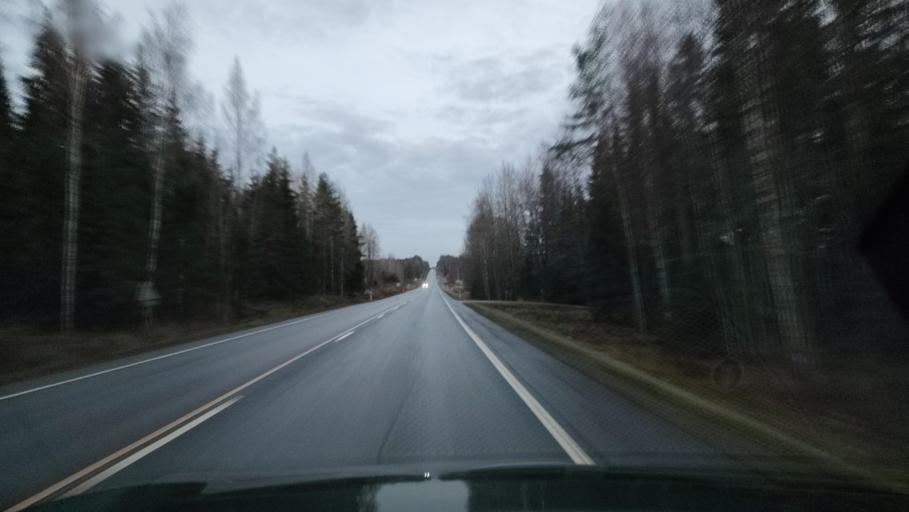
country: FI
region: Ostrobothnia
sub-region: Vaasa
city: Ristinummi
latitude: 62.9753
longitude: 21.7688
